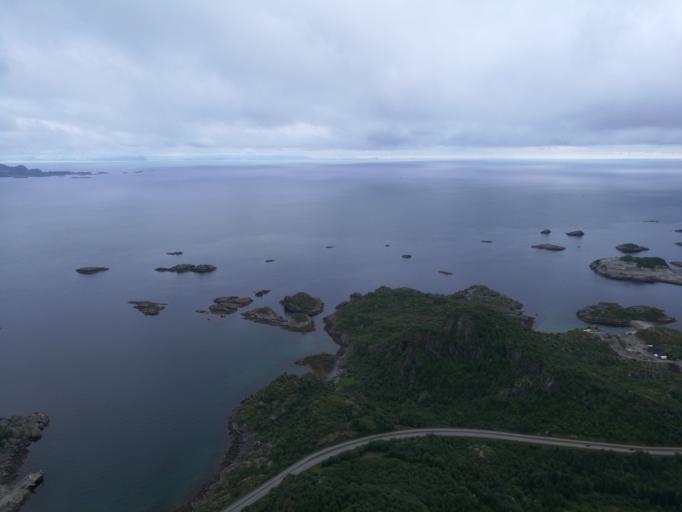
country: NO
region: Nordland
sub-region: Vagan
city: Kabelvag
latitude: 68.2266
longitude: 14.5098
